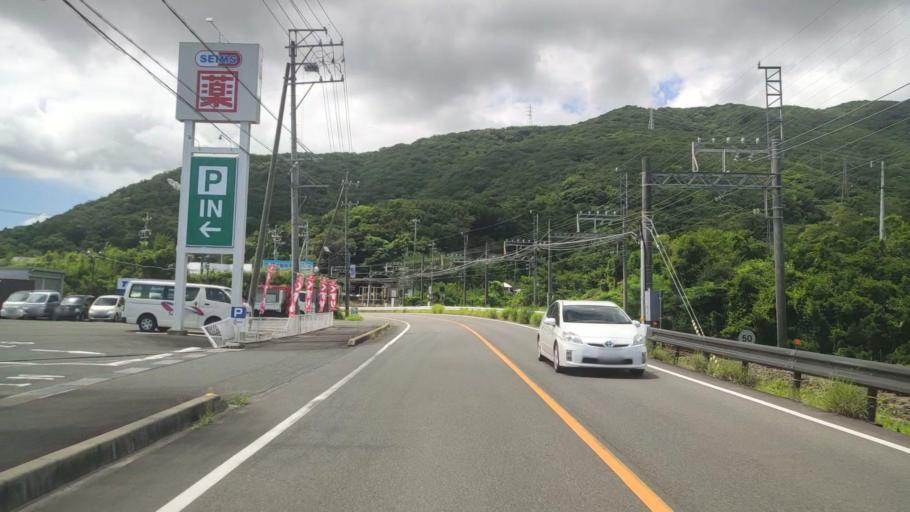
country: JP
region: Mie
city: Toba
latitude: 34.4648
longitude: 136.8396
